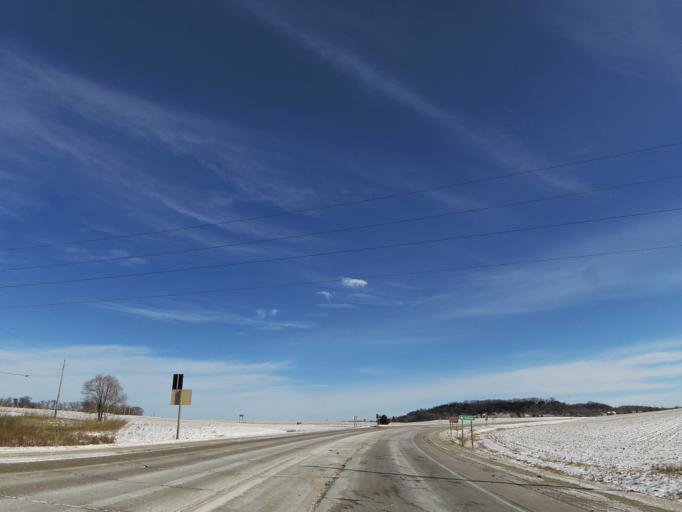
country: US
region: Wisconsin
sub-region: Pierce County
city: Prescott
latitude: 44.7746
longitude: -92.7792
